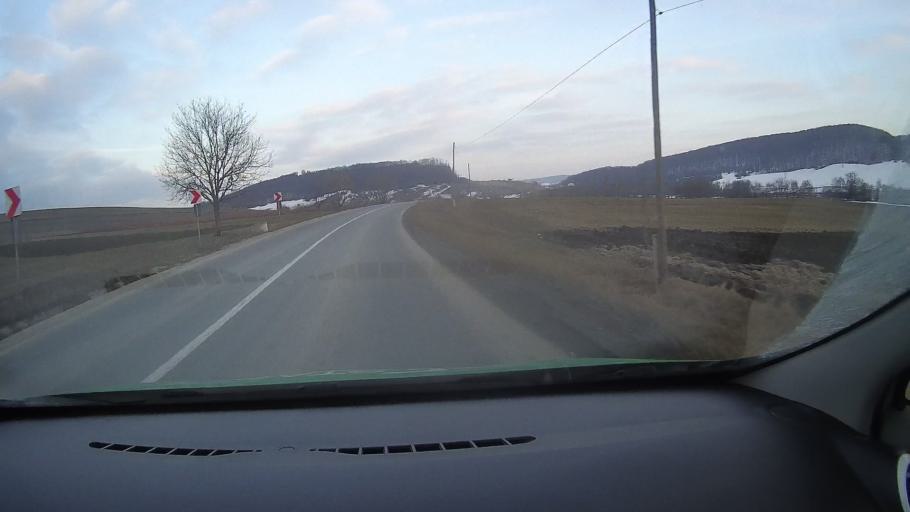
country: RO
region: Harghita
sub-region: Comuna Lupeni
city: Lupeni
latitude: 46.3613
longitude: 25.1826
